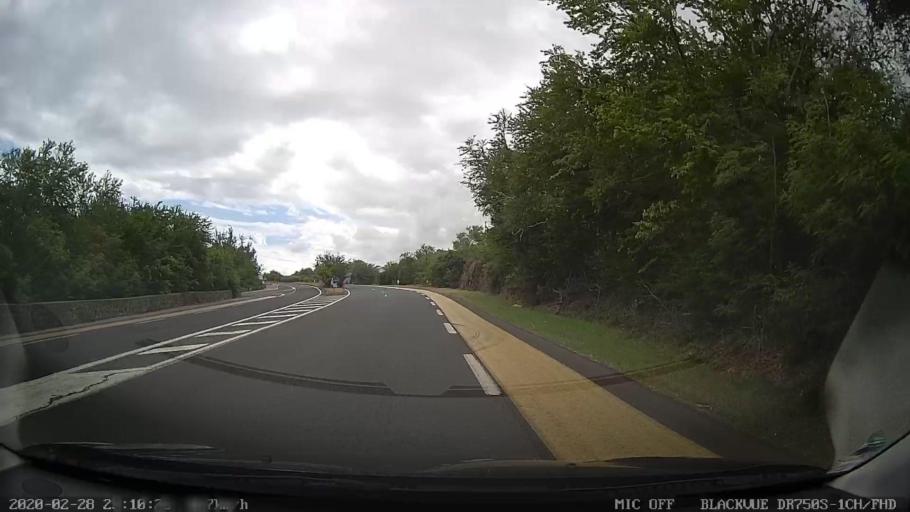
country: RE
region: Reunion
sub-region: Reunion
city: Trois-Bassins
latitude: -21.1189
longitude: 55.2604
